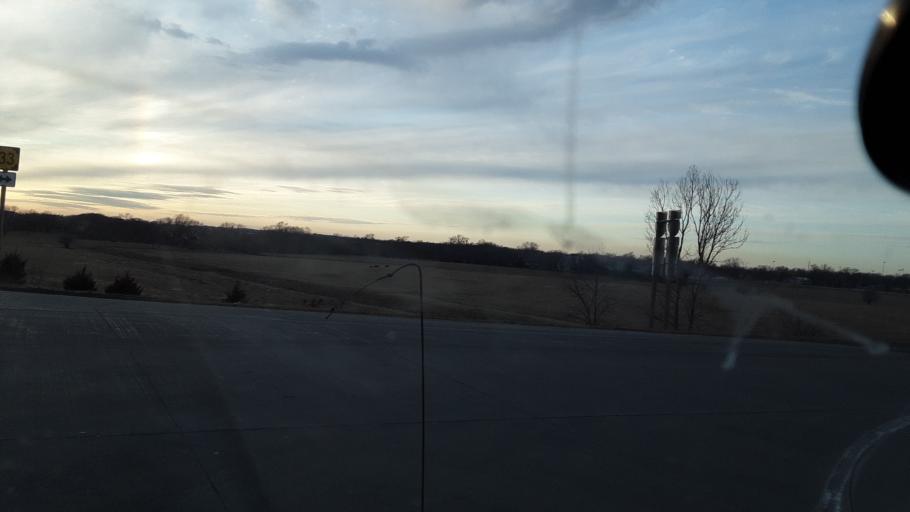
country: US
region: Kansas
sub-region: Franklin County
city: Wellsville
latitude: 38.7057
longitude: -95.0747
